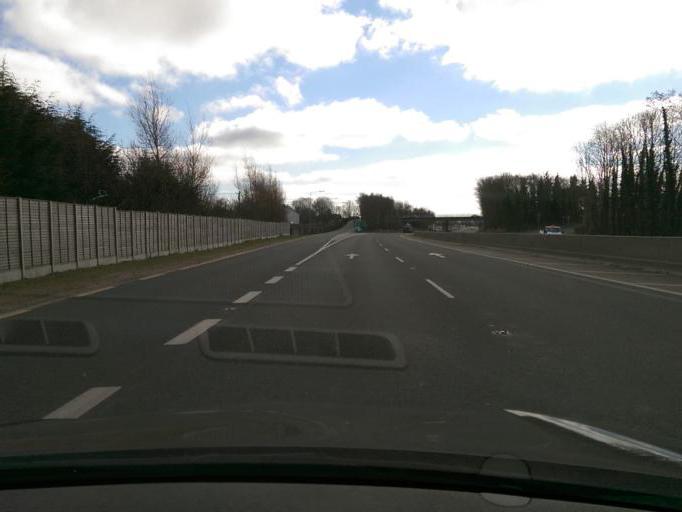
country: IE
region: Leinster
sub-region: An Iarmhi
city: Athlone
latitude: 53.4326
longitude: -7.9286
